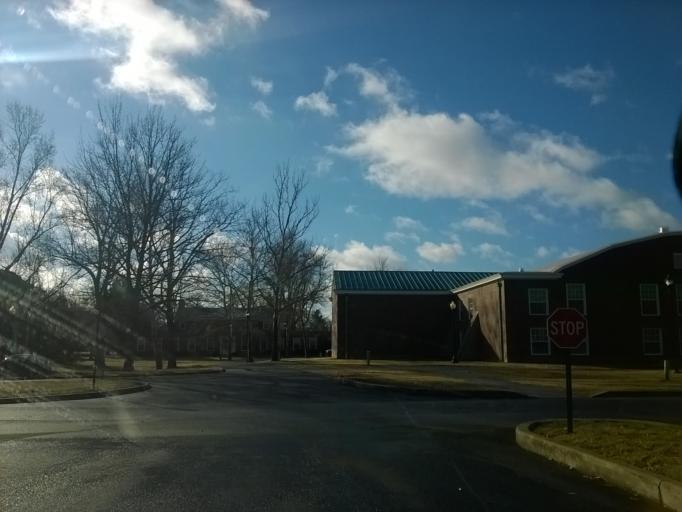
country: US
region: Indiana
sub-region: Jefferson County
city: Hanover
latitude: 38.7151
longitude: -85.4594
